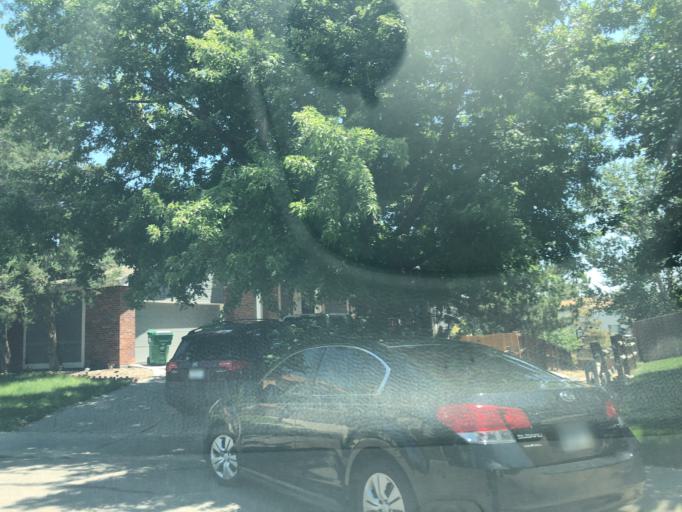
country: US
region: Colorado
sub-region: Arapahoe County
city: Dove Valley
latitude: 39.6171
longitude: -104.7547
